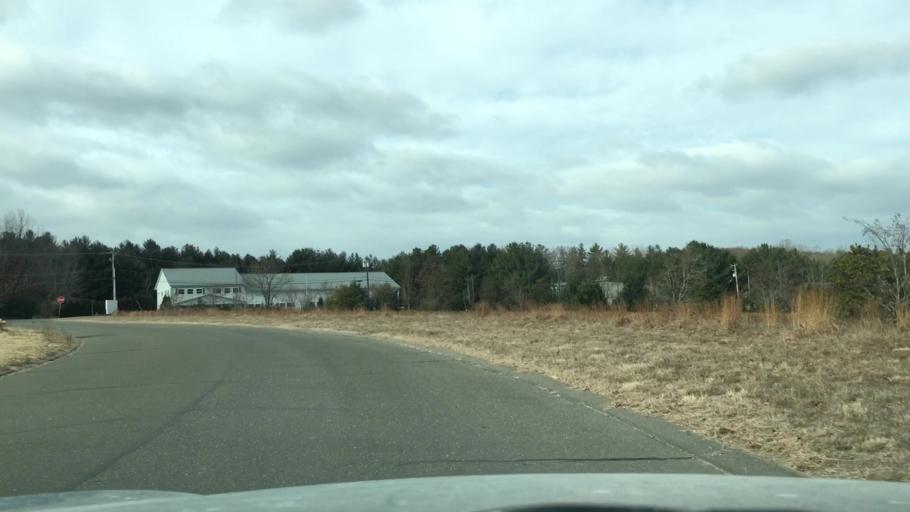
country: US
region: Massachusetts
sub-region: Hampden County
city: Southwick
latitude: 42.0699
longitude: -72.7435
